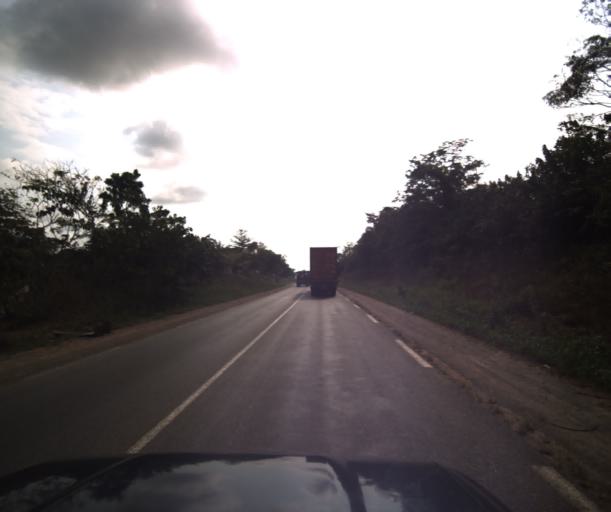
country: CM
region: Littoral
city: Edea
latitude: 3.9495
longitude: 10.0222
